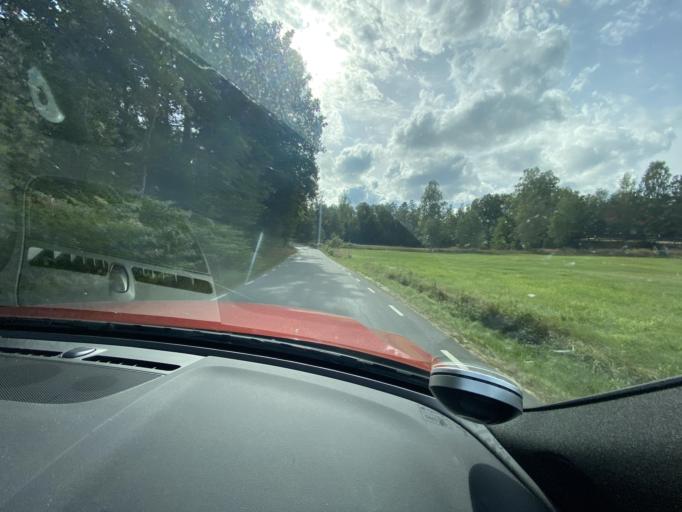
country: SE
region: Skane
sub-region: Hassleholms Kommun
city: Bjarnum
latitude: 56.3602
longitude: 13.8007
